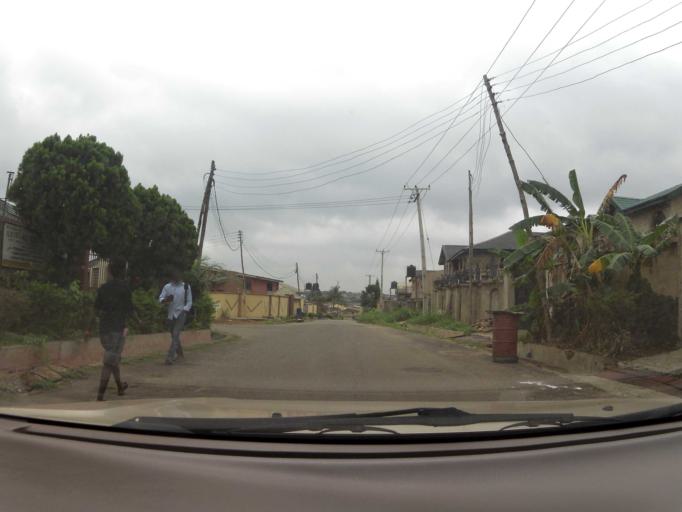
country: NG
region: Oyo
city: Ibadan
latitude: 7.4260
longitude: 3.9389
